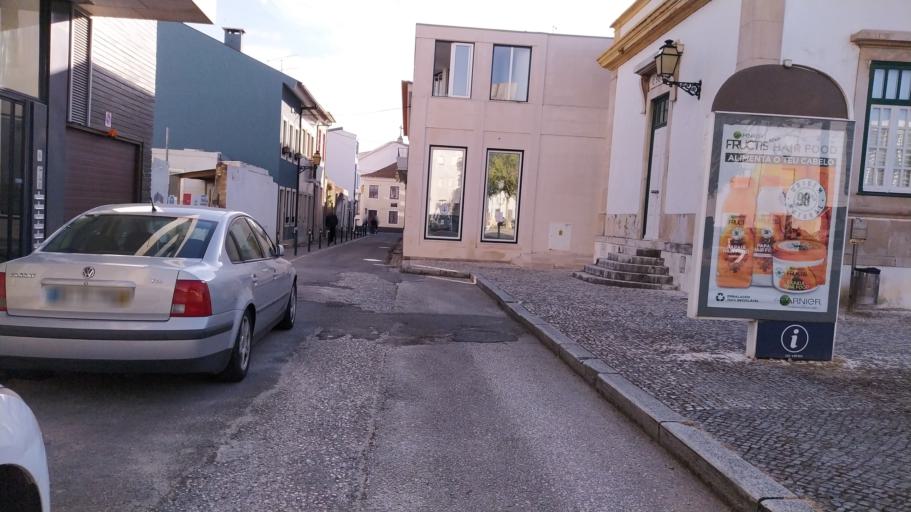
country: PT
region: Aveiro
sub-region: Aveiro
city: Aveiro
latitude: 40.6431
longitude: -8.6520
